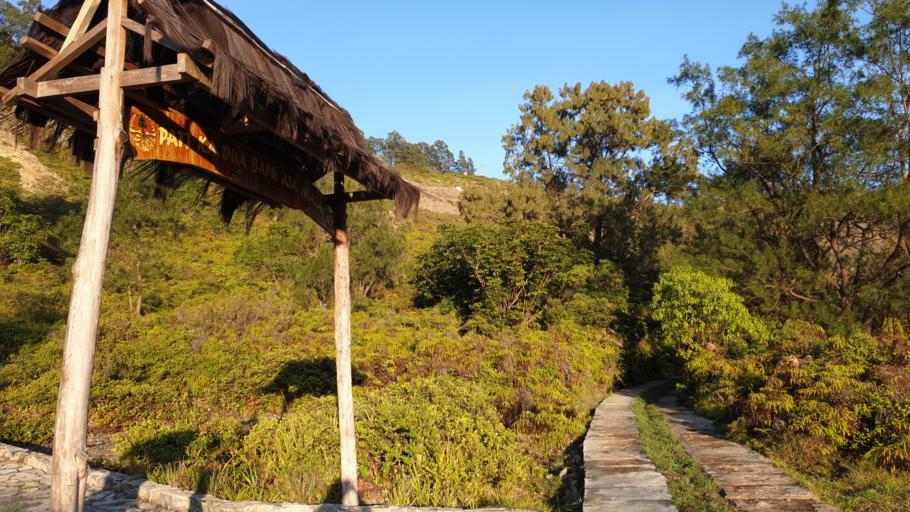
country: ID
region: East Nusa Tenggara
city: Koanara
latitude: -8.7681
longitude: 121.8130
